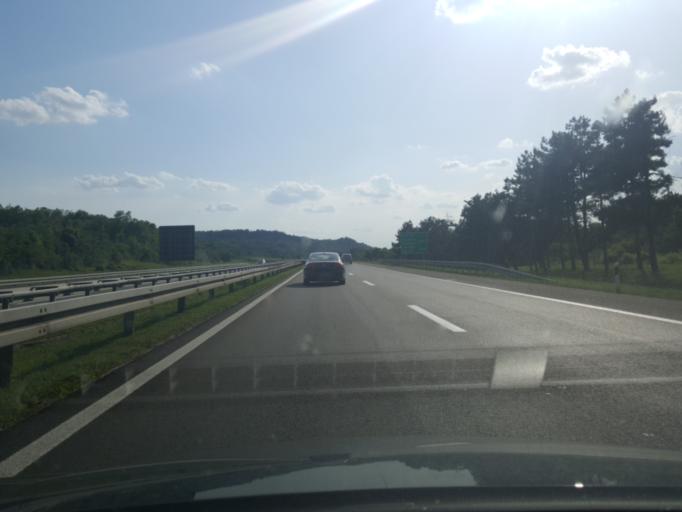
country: RS
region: Central Serbia
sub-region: Belgrade
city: Grocka
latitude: 44.5828
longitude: 20.8090
